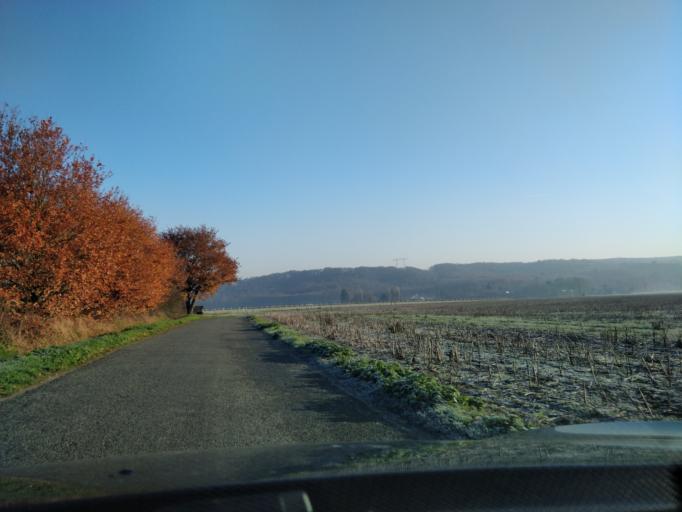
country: FR
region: Ile-de-France
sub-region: Departement de l'Essonne
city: Forges-les-Bains
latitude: 48.6322
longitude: 2.1063
